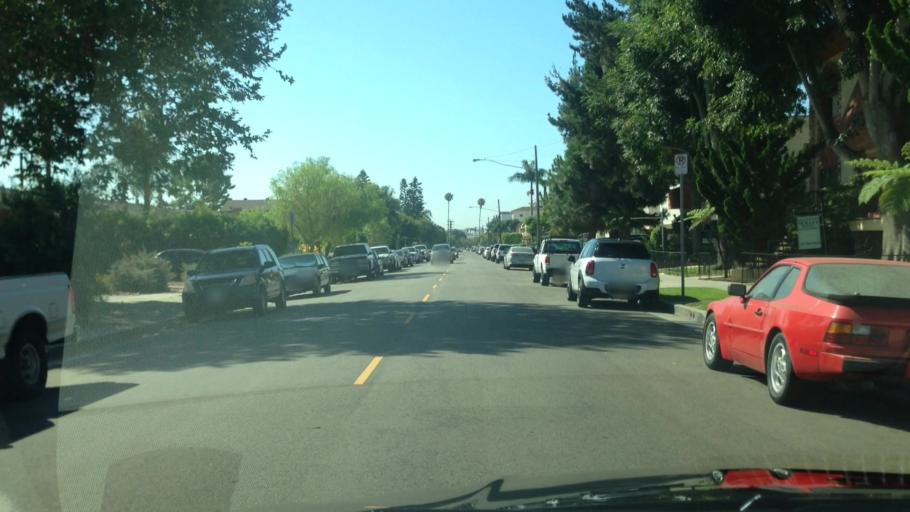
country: US
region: California
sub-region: Los Angeles County
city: Culver City
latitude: 34.0038
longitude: -118.4208
